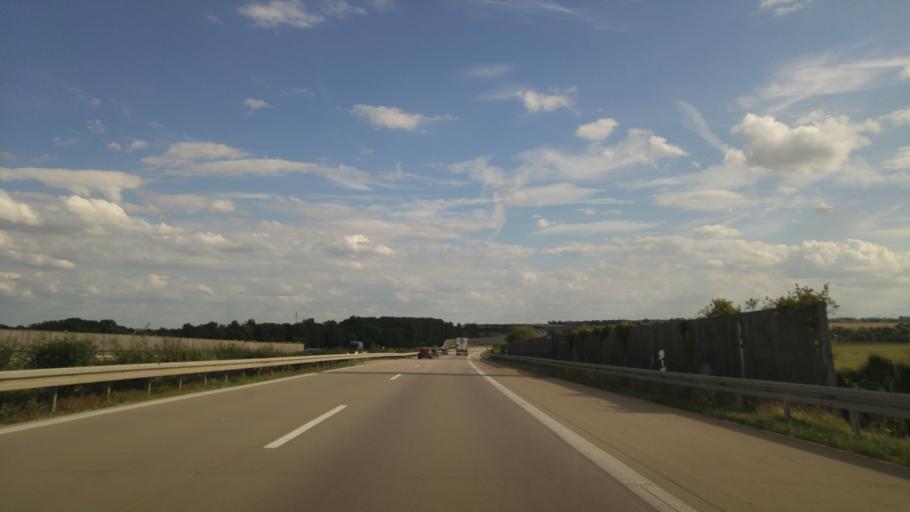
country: DE
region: Saxony-Anhalt
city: Bad Lauchstadt
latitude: 51.3816
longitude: 11.9114
